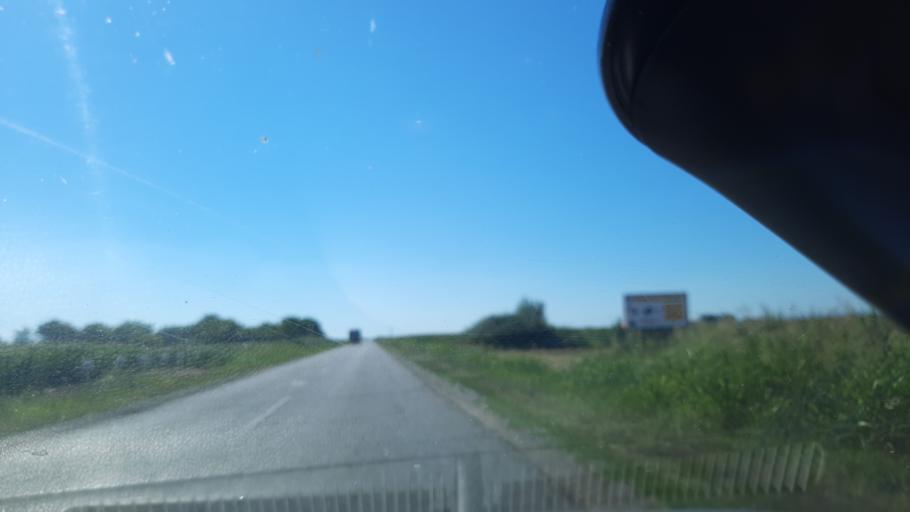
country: RS
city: Simanovci
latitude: 44.8782
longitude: 20.0643
